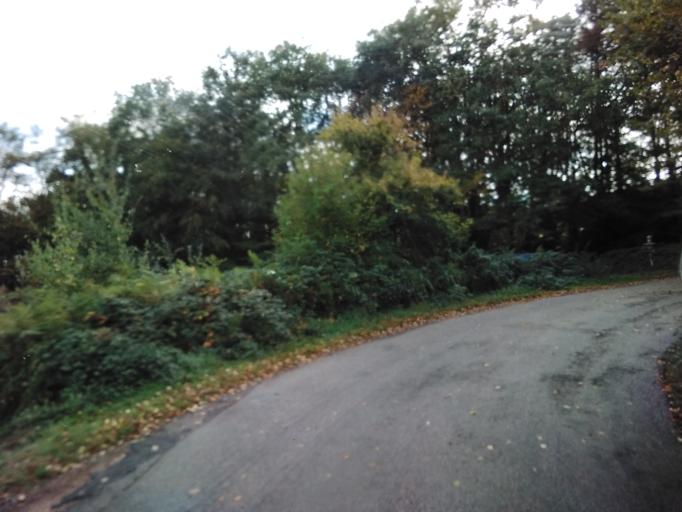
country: FR
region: Bourgogne
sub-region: Departement de la Nievre
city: Lormes
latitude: 47.3007
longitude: 3.8945
